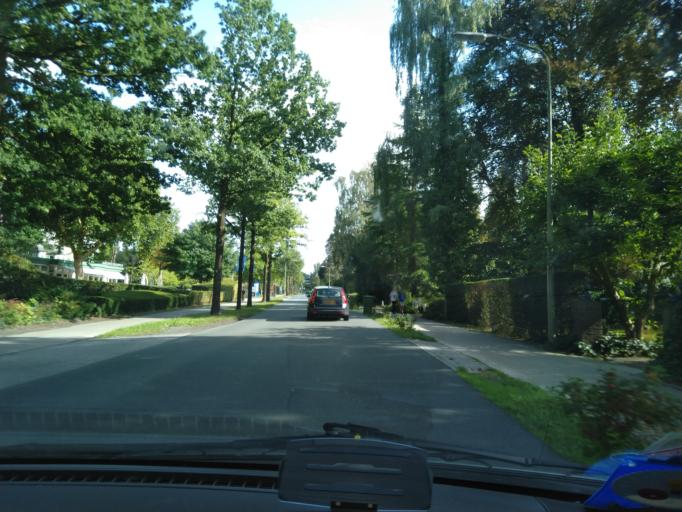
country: NL
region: Groningen
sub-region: Gemeente Haren
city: Haren
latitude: 53.1616
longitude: 6.5578
